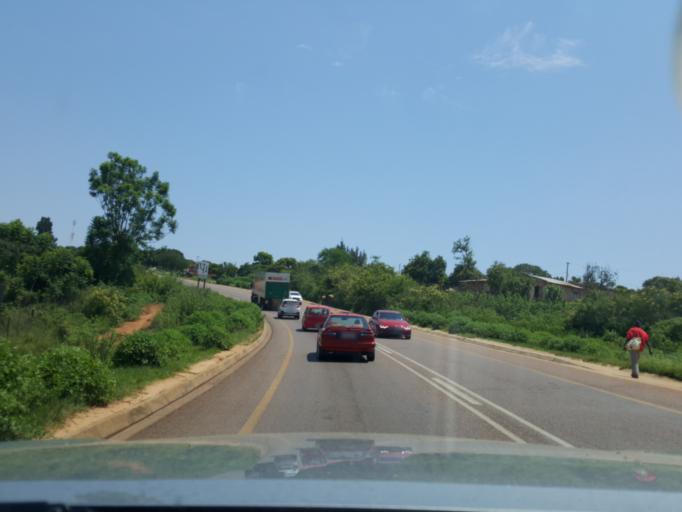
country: ZA
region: Limpopo
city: Thulamahashi
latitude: -24.9434
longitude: 31.1277
